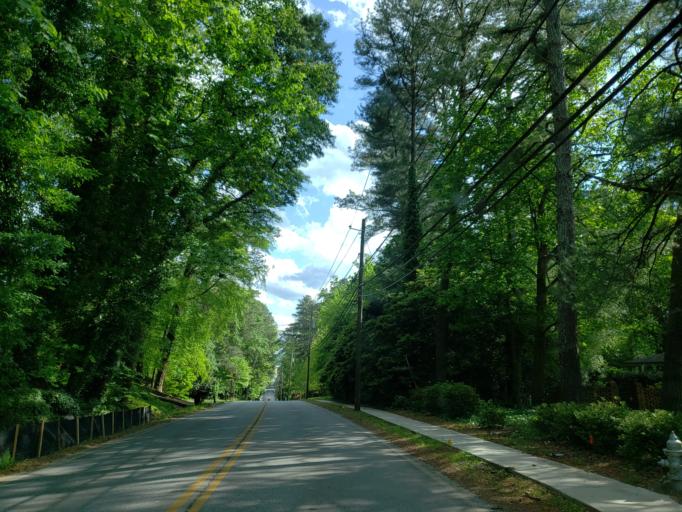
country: US
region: Georgia
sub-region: DeKalb County
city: Chamblee
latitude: 33.8526
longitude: -84.2826
